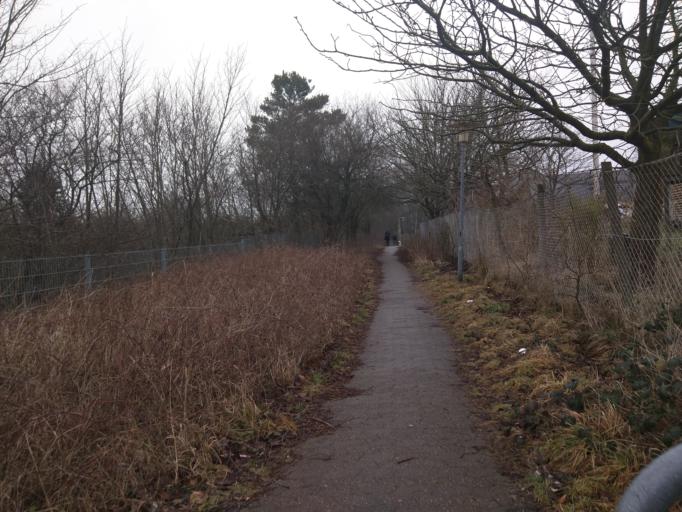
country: DK
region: South Denmark
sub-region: Fredericia Kommune
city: Snoghoj
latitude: 55.5462
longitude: 9.7098
